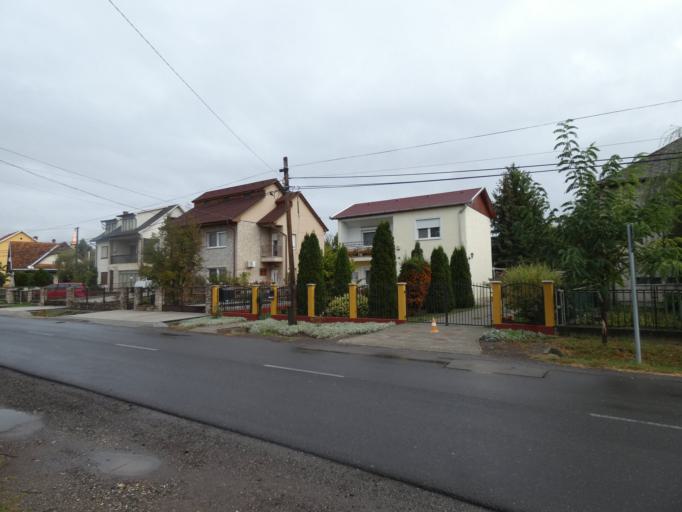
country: HU
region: Heves
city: Rozsaszentmarton
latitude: 47.7871
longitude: 19.7417
